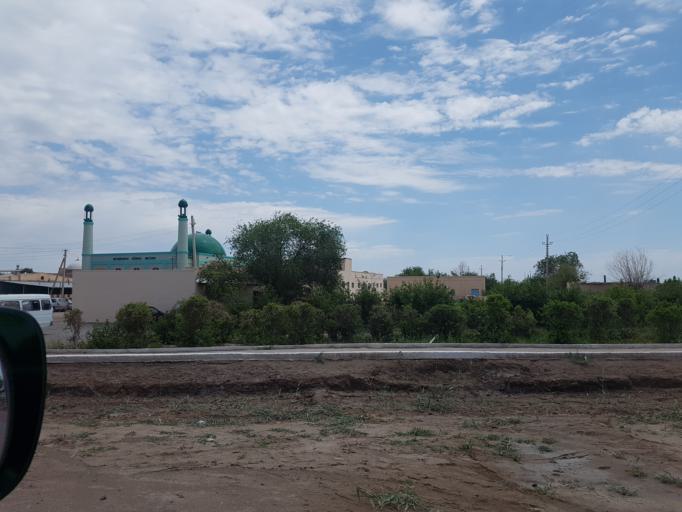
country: TM
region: Dasoguz
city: Koeneuergench
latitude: 42.3223
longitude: 59.1400
